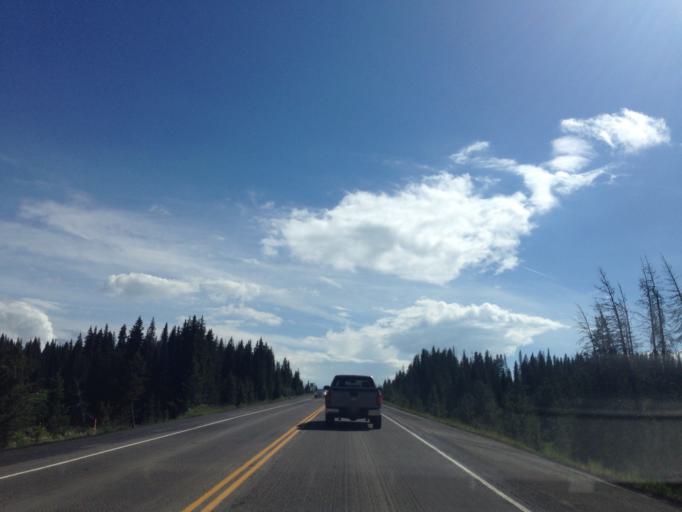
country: US
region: Colorado
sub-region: Routt County
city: Steamboat Springs
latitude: 40.3724
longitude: -106.7383
